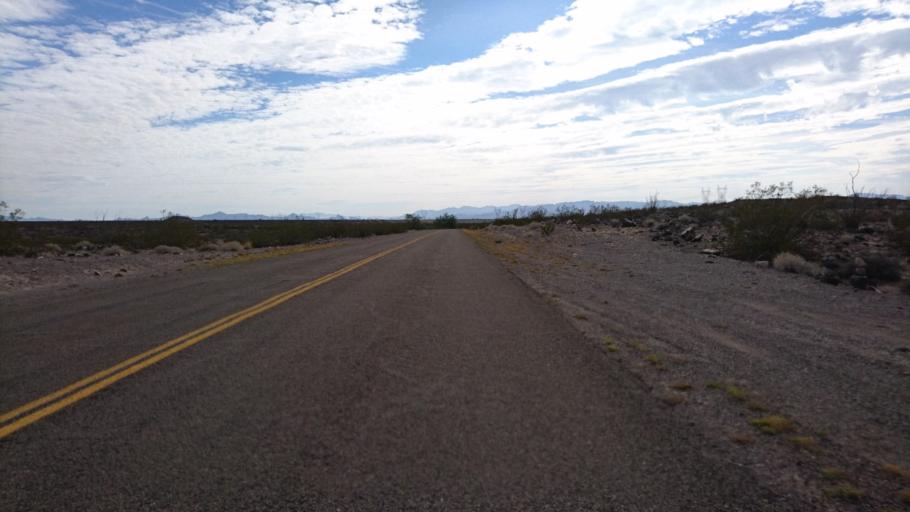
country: US
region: Arizona
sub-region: Mohave County
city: Mohave Valley
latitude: 34.8774
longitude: -114.4363
